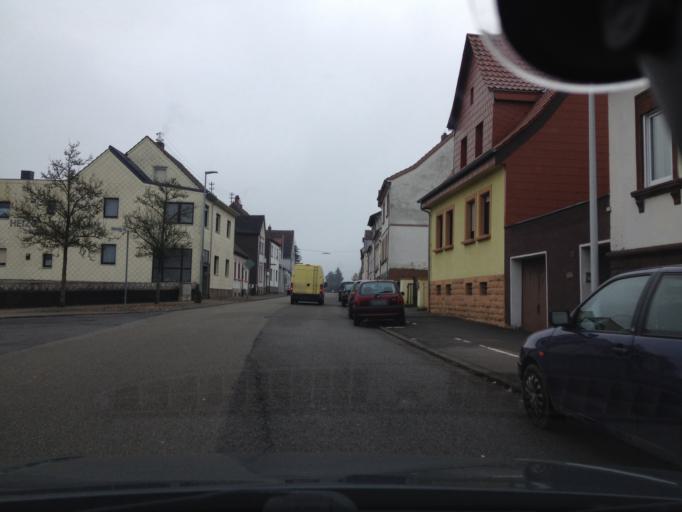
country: DE
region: Saarland
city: Bexbach
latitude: 49.3522
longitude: 7.2497
